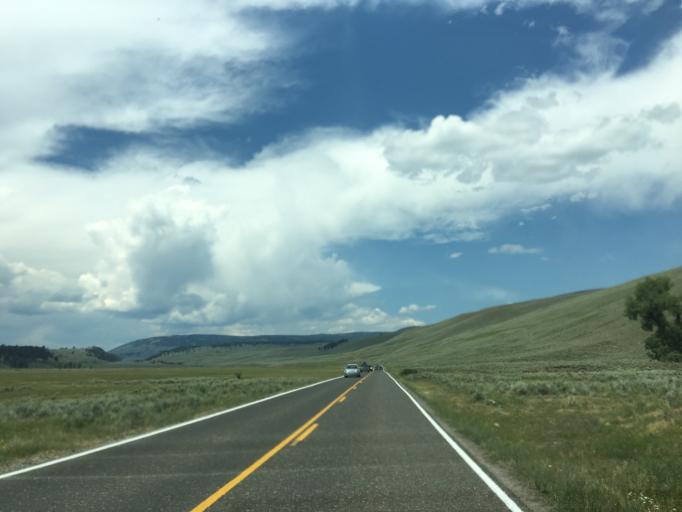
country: US
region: Montana
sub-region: Park County
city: Livingston
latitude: 44.8951
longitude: -110.2360
